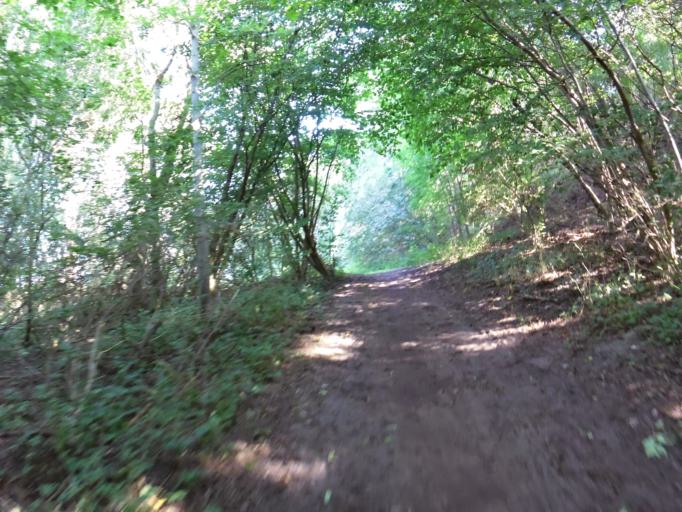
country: DE
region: Mecklenburg-Vorpommern
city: Loddin
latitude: 53.9579
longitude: 14.0408
